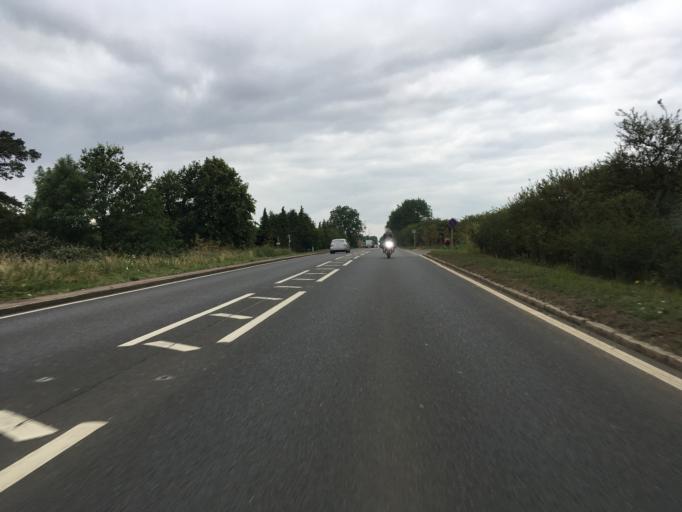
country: GB
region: England
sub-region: Central Bedfordshire
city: Potsgrove
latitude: 51.9606
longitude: -0.6371
